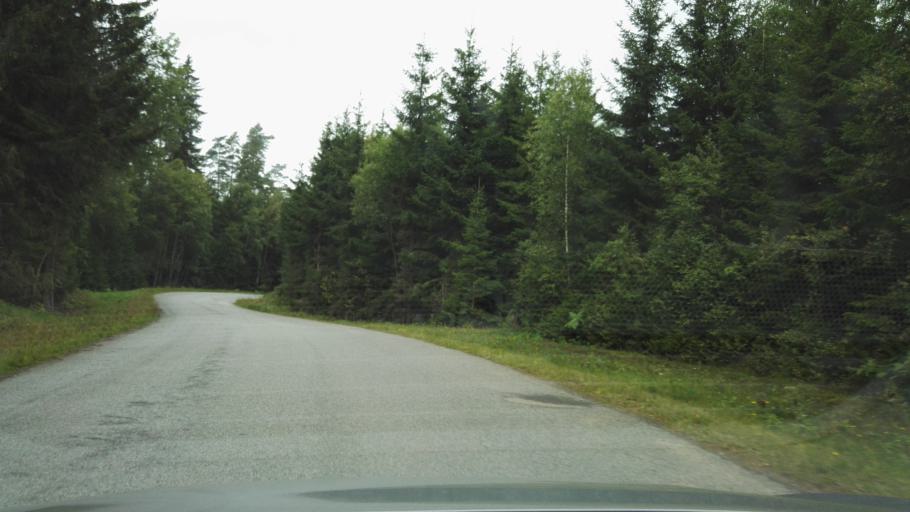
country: SE
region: Joenkoeping
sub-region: Vetlanda Kommun
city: Landsbro
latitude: 57.2803
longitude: 14.8329
